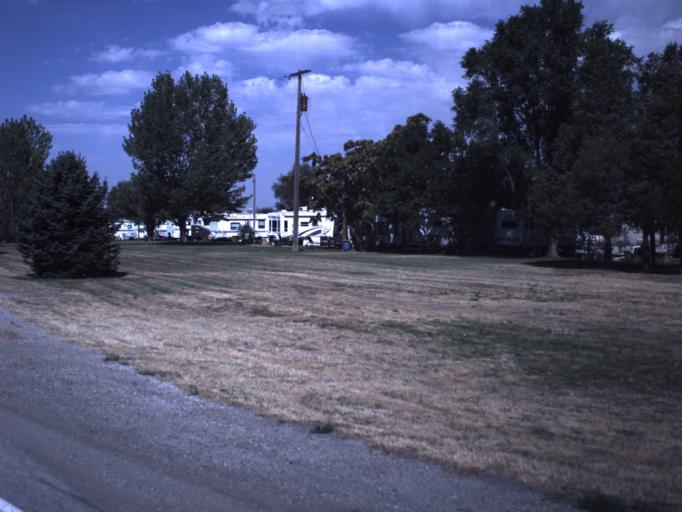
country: US
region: Utah
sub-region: Box Elder County
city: Willard
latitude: 41.4224
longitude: -112.0361
